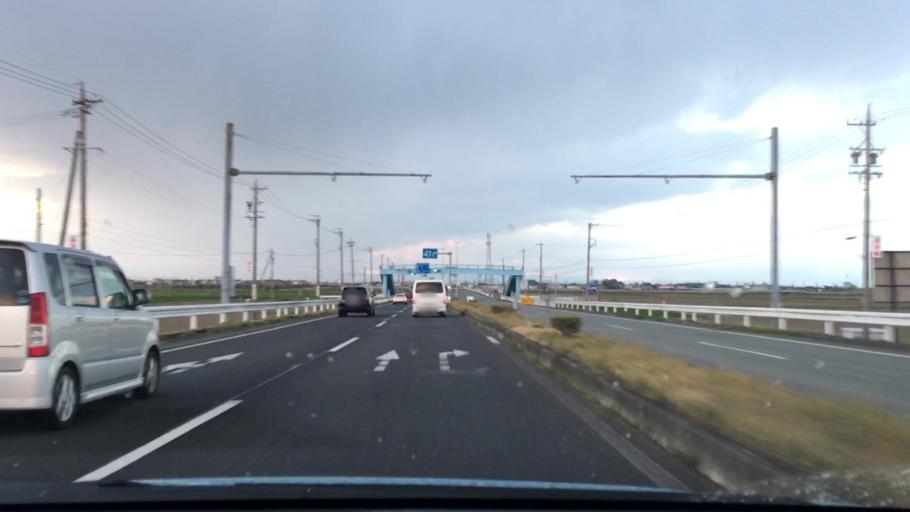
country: JP
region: Mie
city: Ise
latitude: 34.5594
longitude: 136.6461
